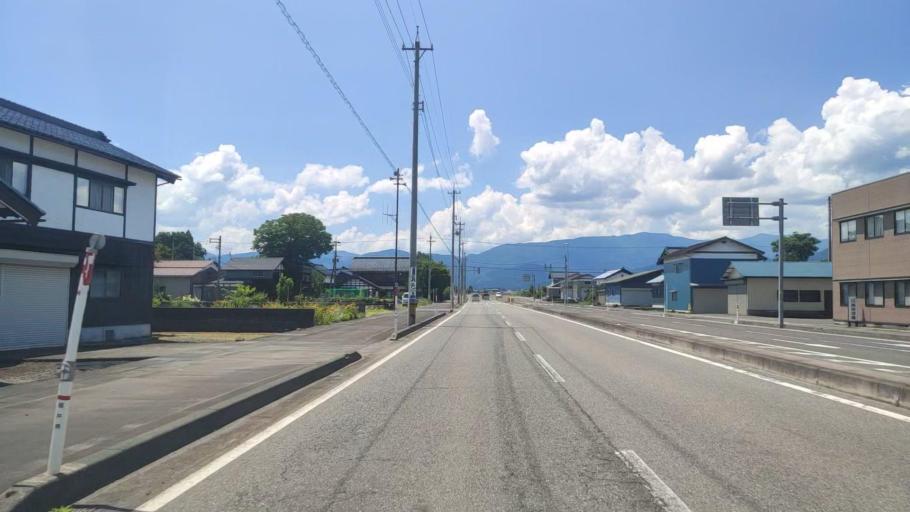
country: JP
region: Fukui
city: Ono
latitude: 36.0032
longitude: 136.5091
